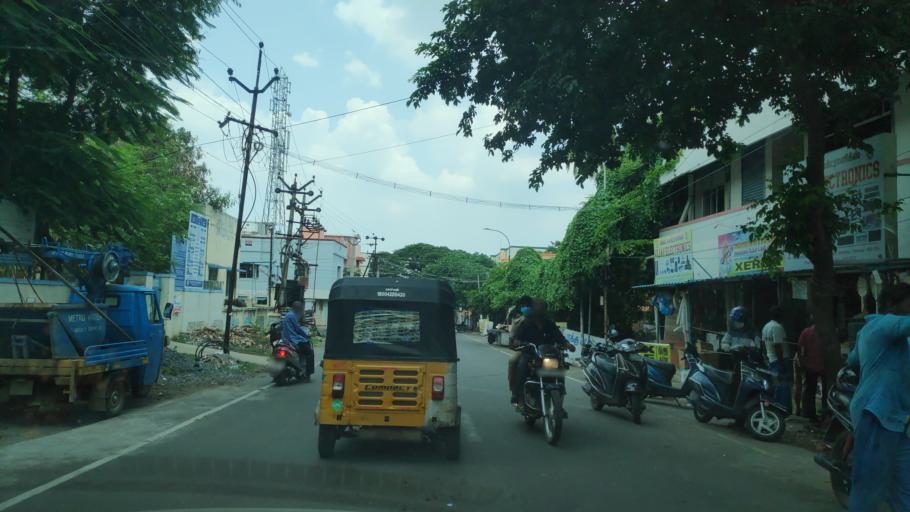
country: IN
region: Tamil Nadu
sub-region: Thiruvallur
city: Ambattur
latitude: 13.1177
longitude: 80.1548
